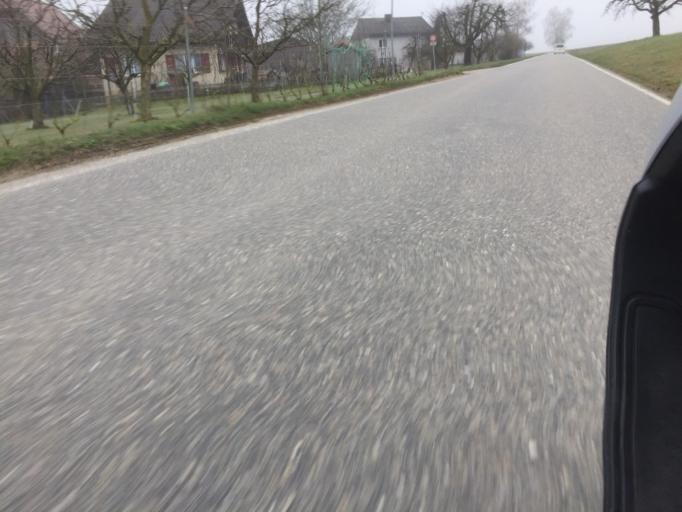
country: CH
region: Bern
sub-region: Seeland District
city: Grossaffoltern
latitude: 47.0826
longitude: 7.3886
